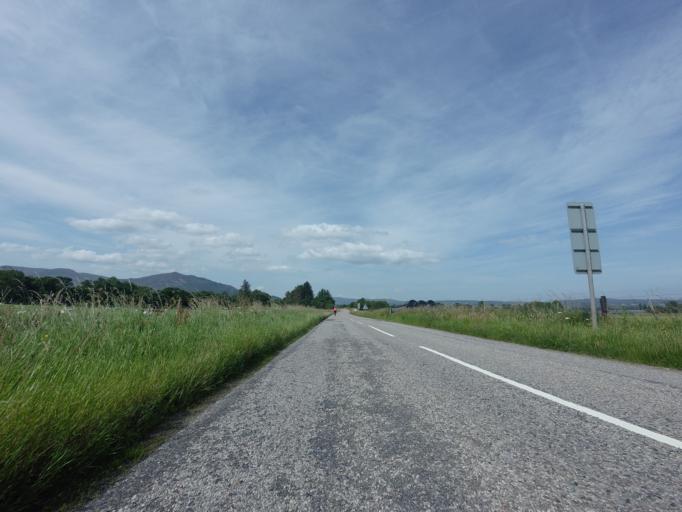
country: GB
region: Scotland
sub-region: Highland
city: Tain
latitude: 57.8352
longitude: -4.1821
